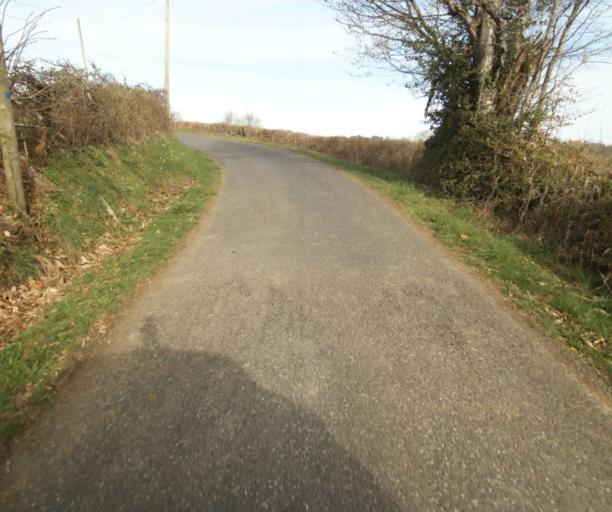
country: FR
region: Limousin
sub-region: Departement de la Correze
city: Chamboulive
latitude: 45.4145
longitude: 1.7850
